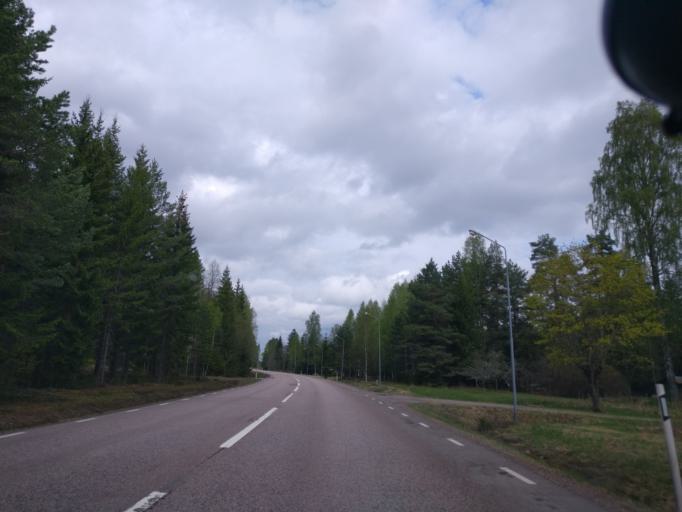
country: SE
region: Vaermland
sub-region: Hagfors Kommun
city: Ekshaerad
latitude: 60.1422
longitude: 13.5250
